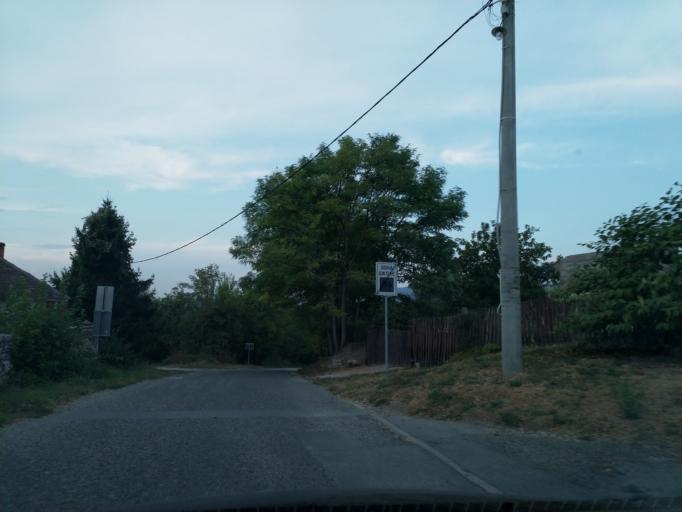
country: RS
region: Central Serbia
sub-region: Pomoravski Okrug
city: Paracin
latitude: 43.8534
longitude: 21.5286
